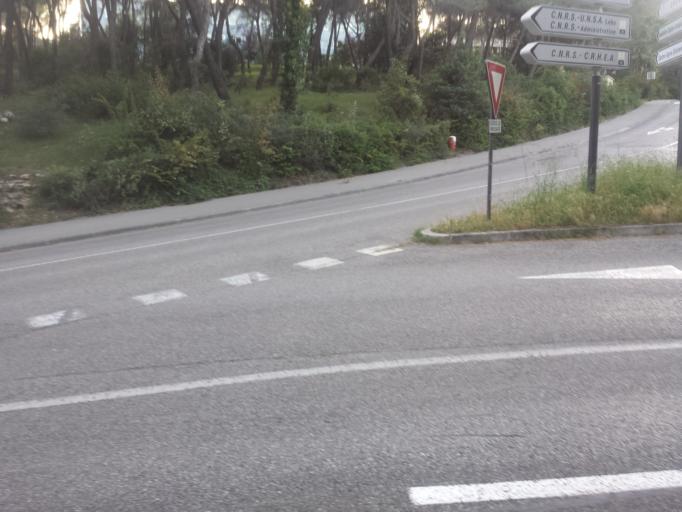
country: FR
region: Provence-Alpes-Cote d'Azur
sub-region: Departement des Alpes-Maritimes
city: Vallauris
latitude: 43.6141
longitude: 7.0541
